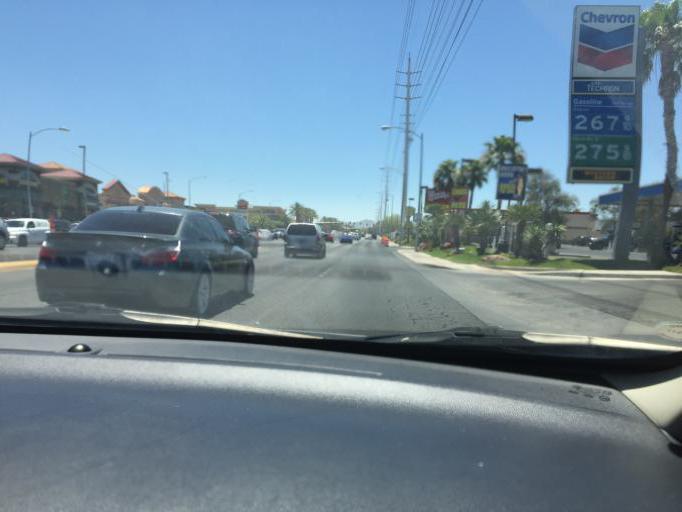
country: US
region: Nevada
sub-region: Clark County
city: Whitney
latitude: 36.0198
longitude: -115.1188
